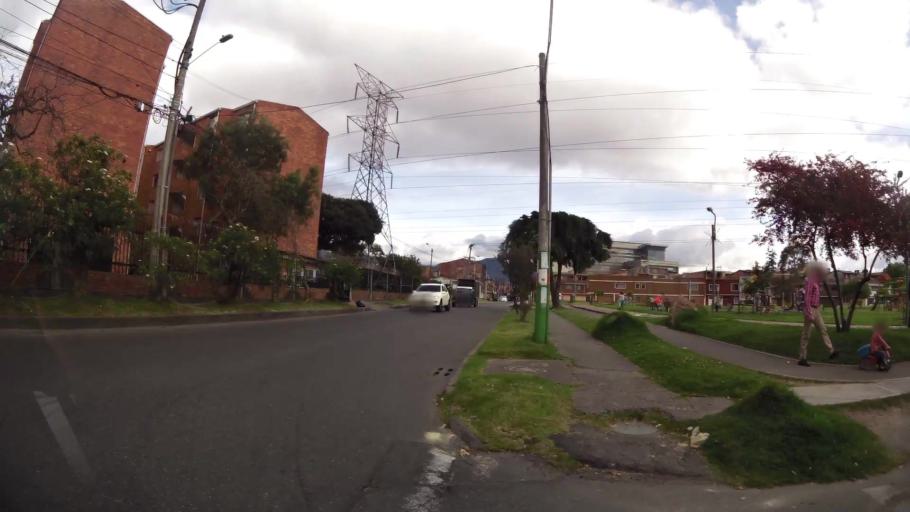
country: CO
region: Bogota D.C.
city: Bogota
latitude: 4.6092
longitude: -74.1314
